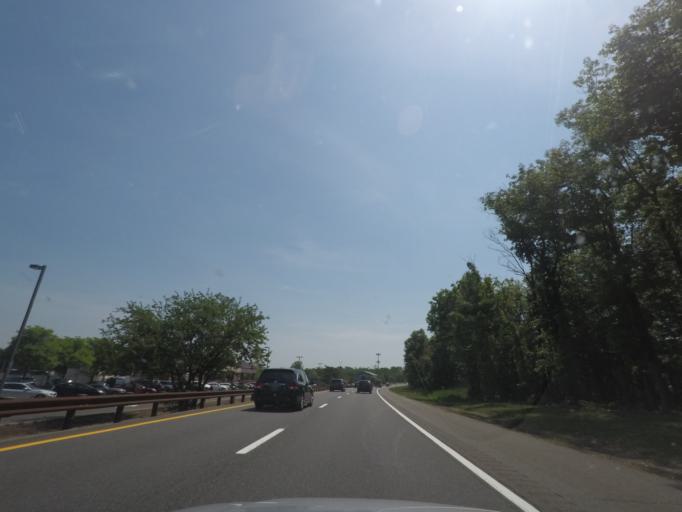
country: US
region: New Jersey
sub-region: Bergen County
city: Woodcliff Lake
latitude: 41.0491
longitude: -74.0668
